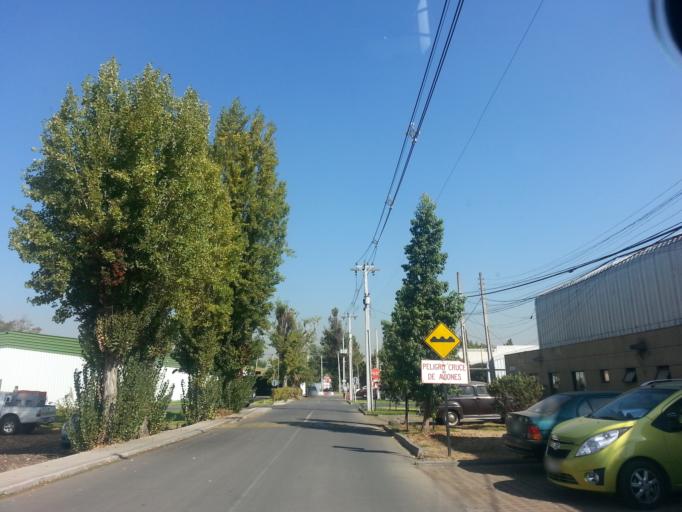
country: CL
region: Santiago Metropolitan
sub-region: Provincia de Santiago
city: Villa Presidente Frei, Nunoa, Santiago, Chile
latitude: -33.4610
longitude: -70.5505
